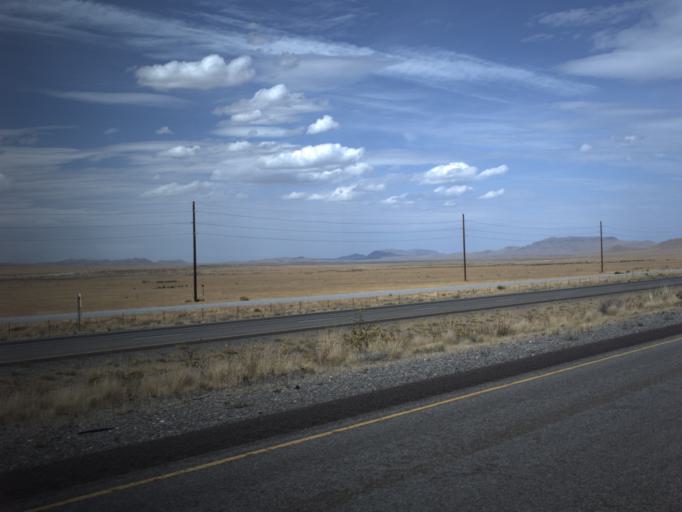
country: US
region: Utah
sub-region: Tooele County
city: Grantsville
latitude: 40.7868
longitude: -112.9598
